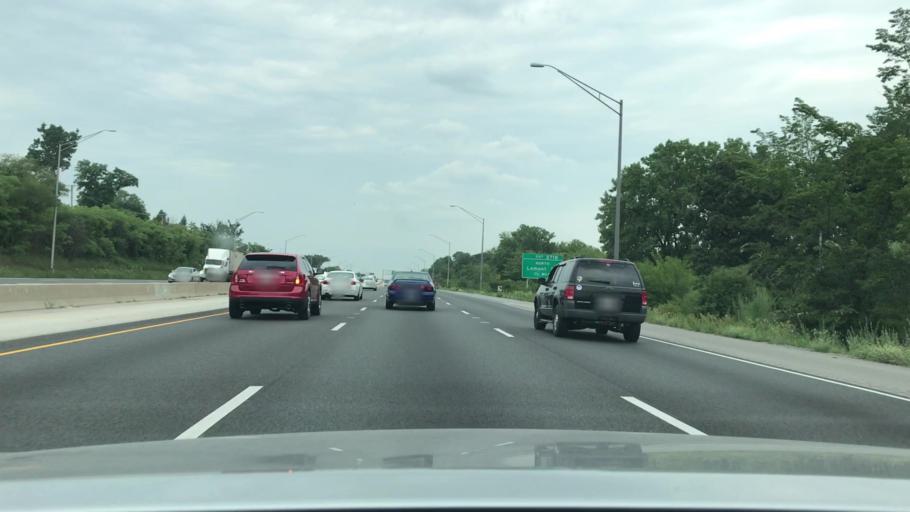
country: US
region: Illinois
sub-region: DuPage County
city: Darien
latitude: 41.7231
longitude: -87.9950
